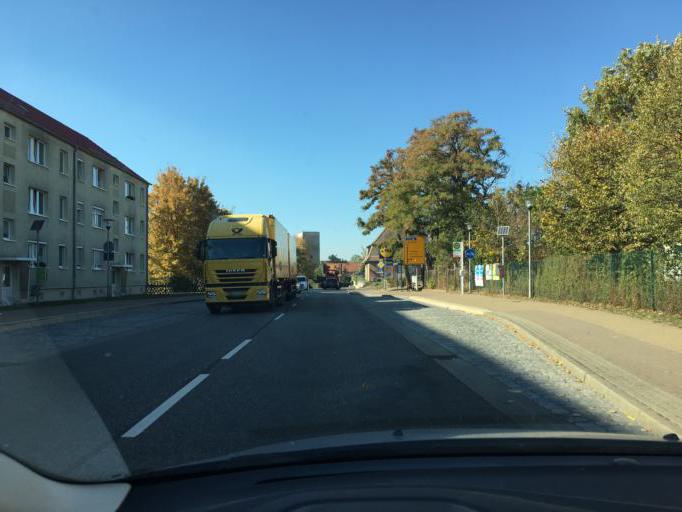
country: DE
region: Saxony-Anhalt
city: Wanzleben
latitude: 52.0639
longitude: 11.4473
